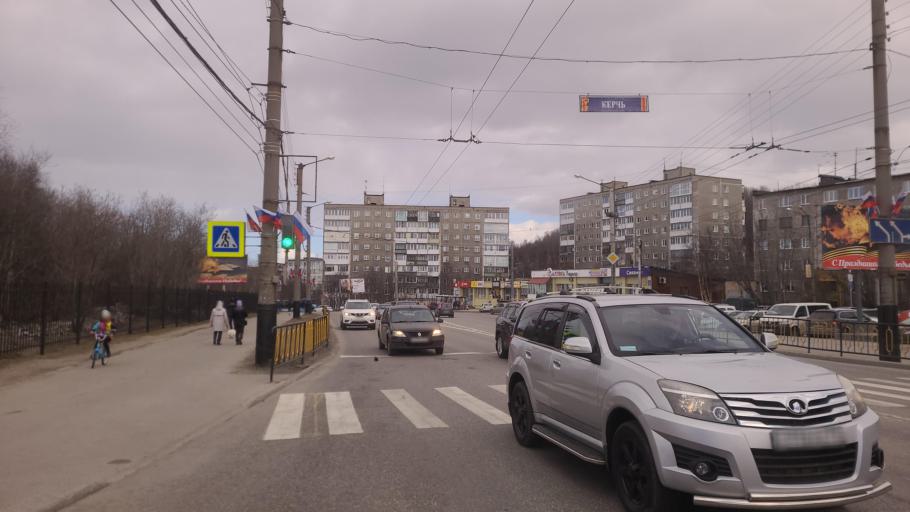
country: RU
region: Murmansk
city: Murmansk
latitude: 68.9904
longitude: 33.0974
